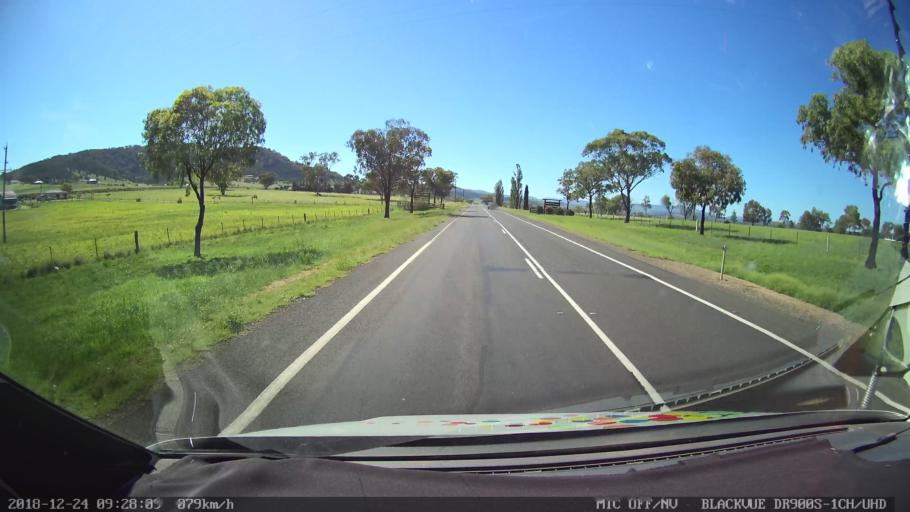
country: AU
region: New South Wales
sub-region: Liverpool Plains
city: Quirindi
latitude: -31.5349
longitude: 150.6864
